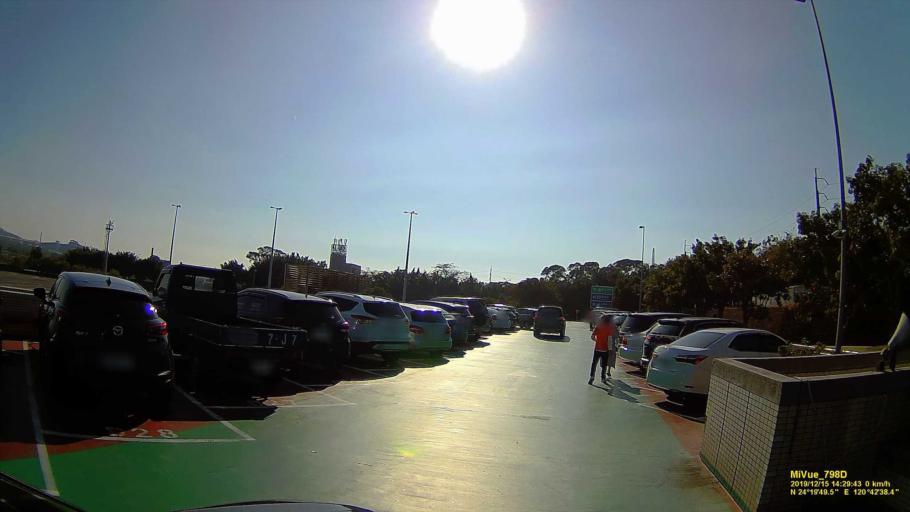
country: TW
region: Taiwan
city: Fengyuan
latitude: 24.3298
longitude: 120.7100
